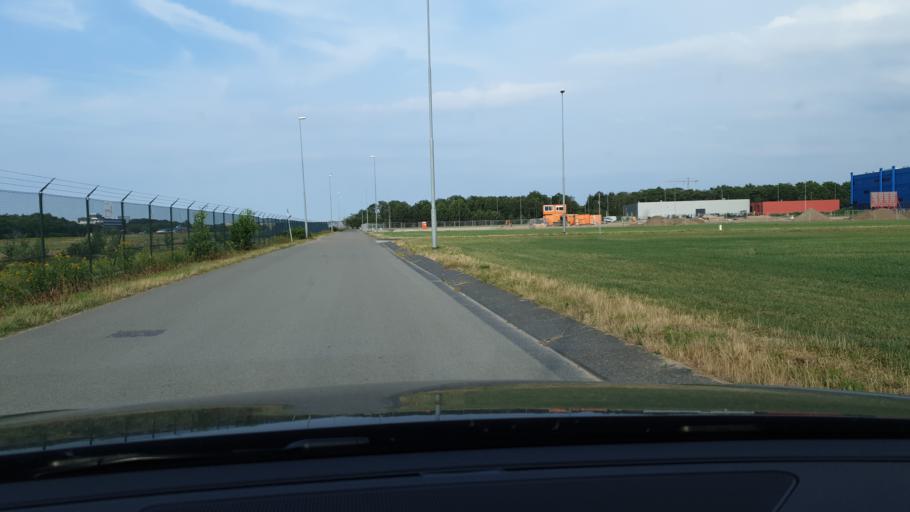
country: NL
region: North Brabant
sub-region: Gemeente Veldhoven
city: Oerle
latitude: 51.4426
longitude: 5.3818
